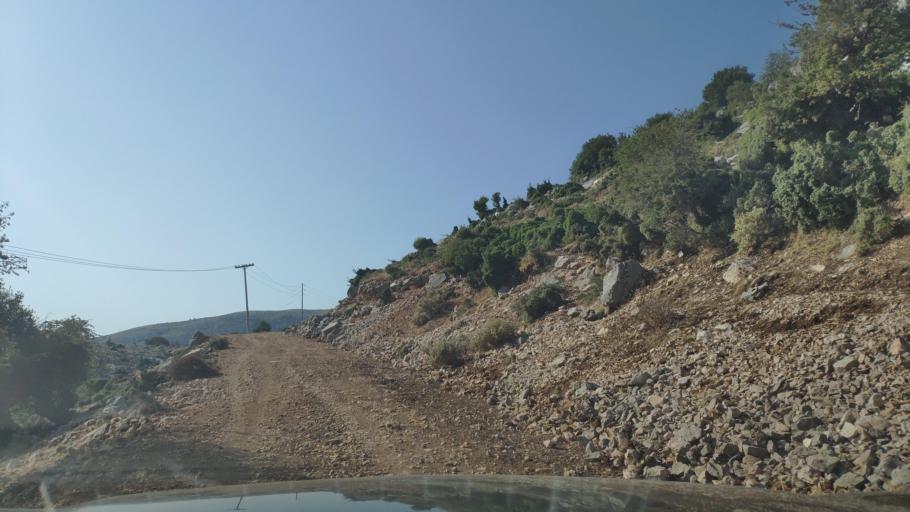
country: GR
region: West Greece
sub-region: Nomos Aitolias kai Akarnanias
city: Monastirakion
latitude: 38.8273
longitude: 20.9788
